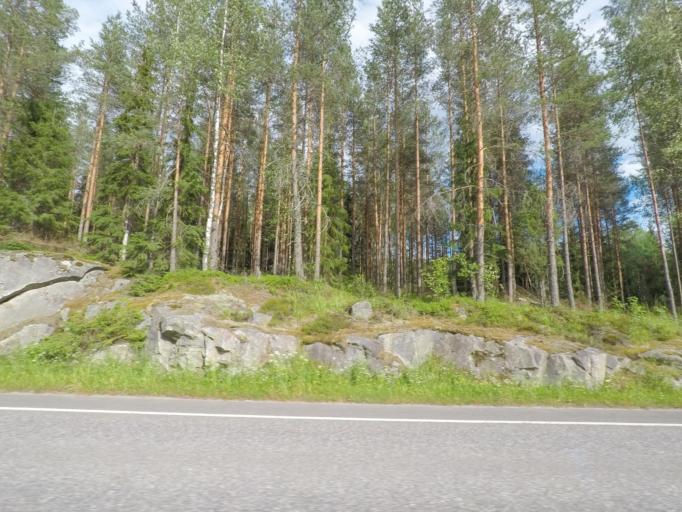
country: FI
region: Paijanne Tavastia
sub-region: Lahti
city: Hollola
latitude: 60.8154
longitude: 25.4824
